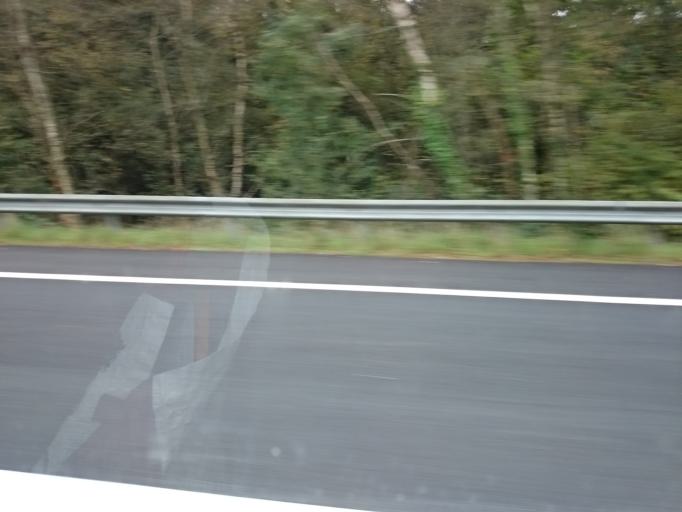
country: FR
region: Brittany
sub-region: Departement des Cotes-d'Armor
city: Plounevez-Moedec
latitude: 48.5489
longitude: -3.4489
